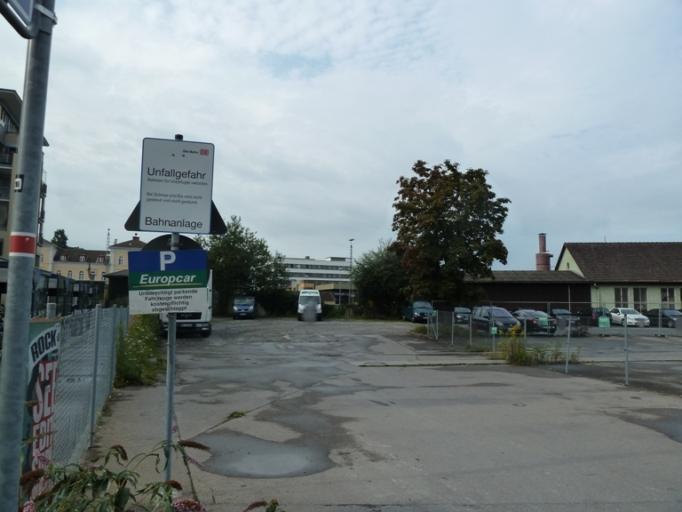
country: DE
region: Baden-Wuerttemberg
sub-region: Tuebingen Region
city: Friedrichshafen
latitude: 47.6542
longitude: 9.4735
